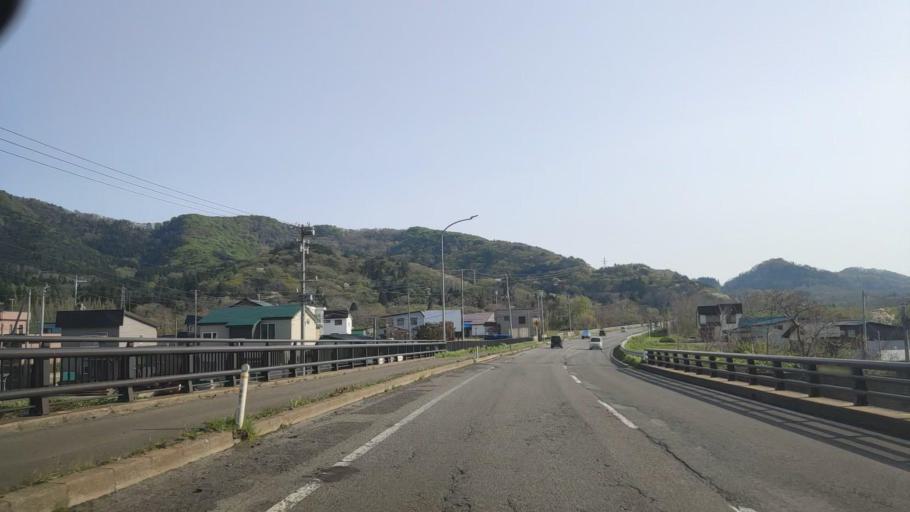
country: JP
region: Aomori
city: Aomori Shi
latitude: 40.8726
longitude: 140.8513
